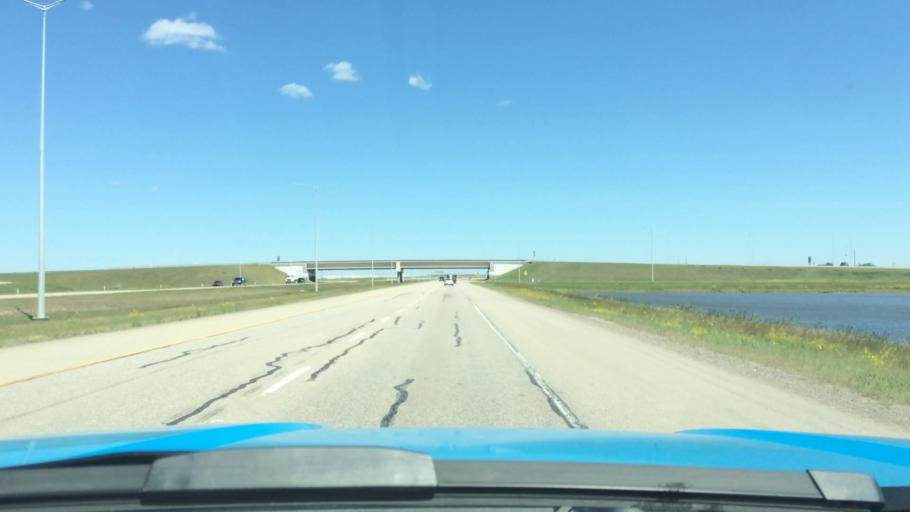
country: CA
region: Alberta
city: Chestermere
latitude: 51.1507
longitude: -113.9210
